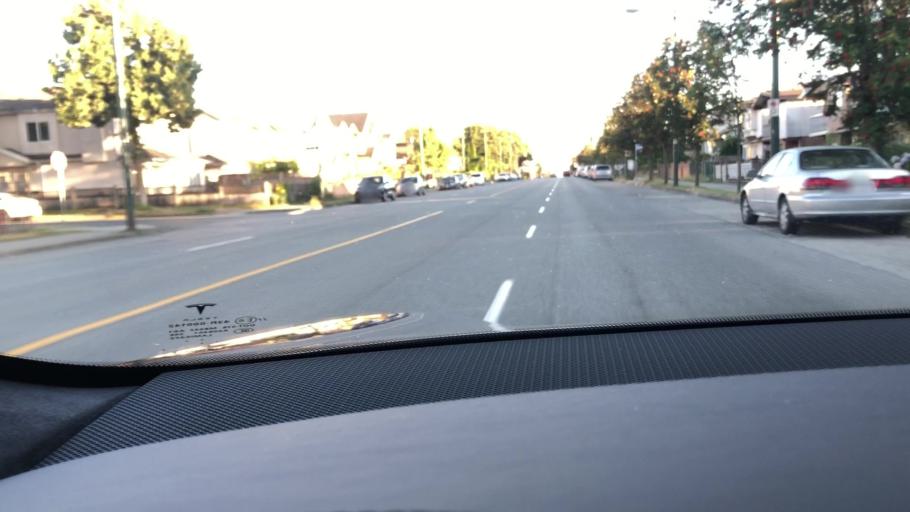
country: CA
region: British Columbia
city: Vancouver
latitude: 49.2298
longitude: -123.0657
